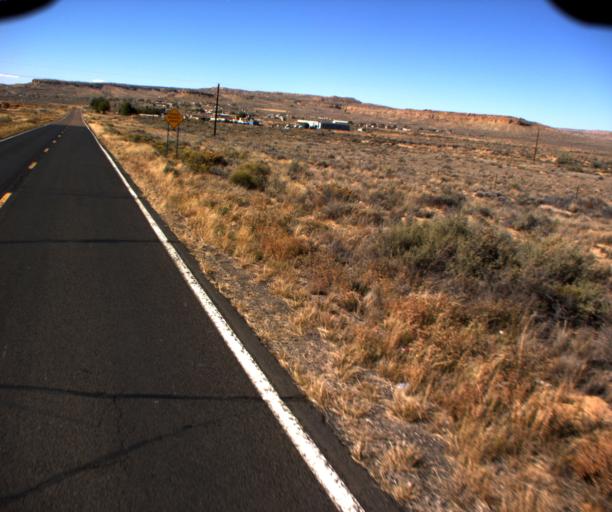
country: US
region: Arizona
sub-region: Navajo County
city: First Mesa
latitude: 35.8732
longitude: -110.5890
